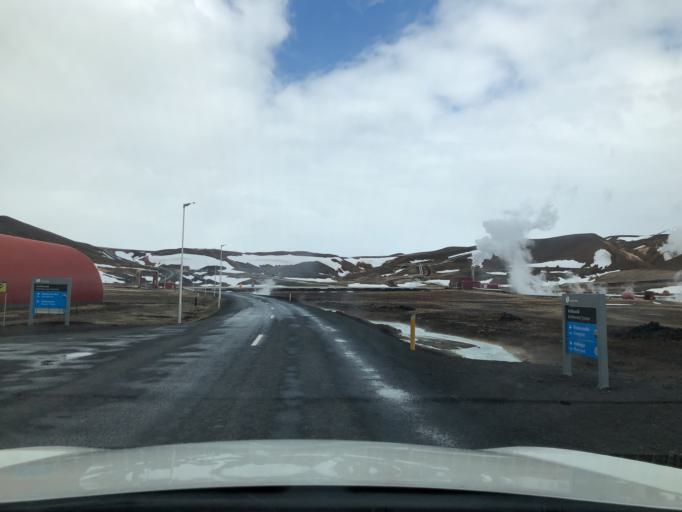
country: IS
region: Northeast
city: Laugar
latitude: 65.7017
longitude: -16.7712
